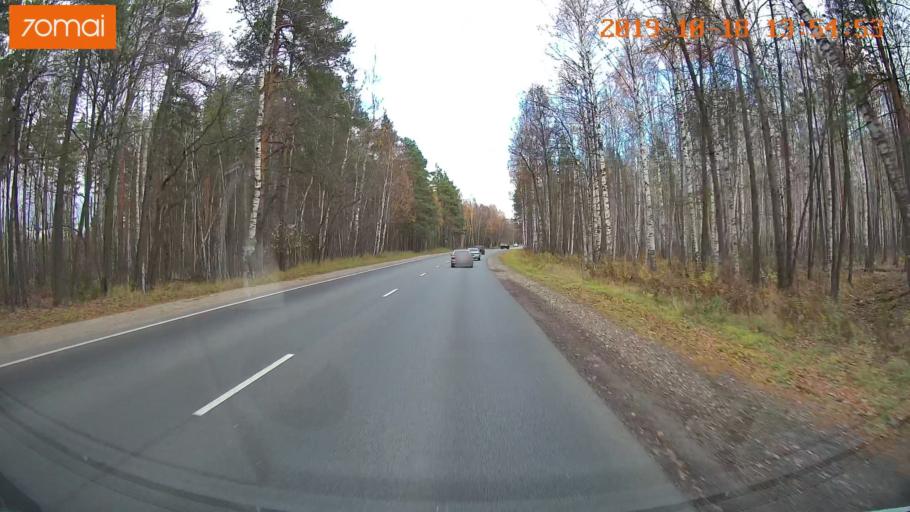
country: RU
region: Rjazan
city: Spas-Klepiki
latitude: 55.0476
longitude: 40.0162
